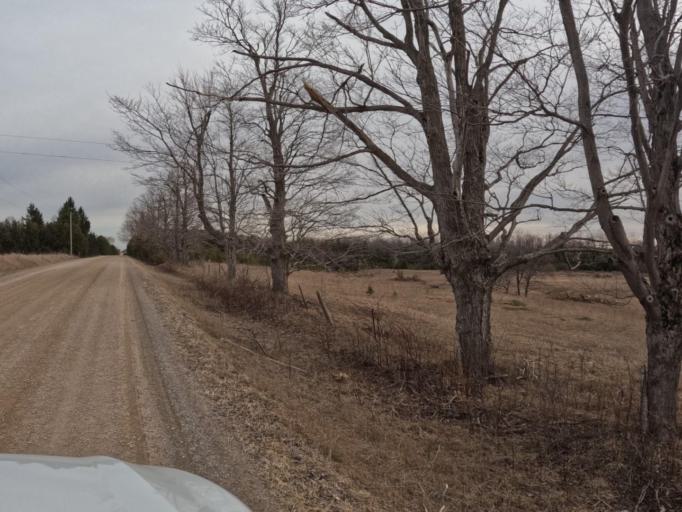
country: CA
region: Ontario
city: Shelburne
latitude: 43.9340
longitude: -80.2585
